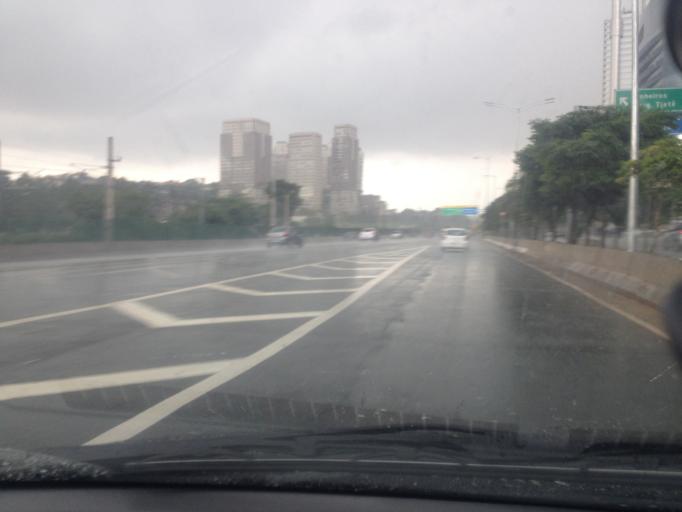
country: BR
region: Sao Paulo
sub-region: Sao Paulo
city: Sao Paulo
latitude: -23.6091
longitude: -46.6978
